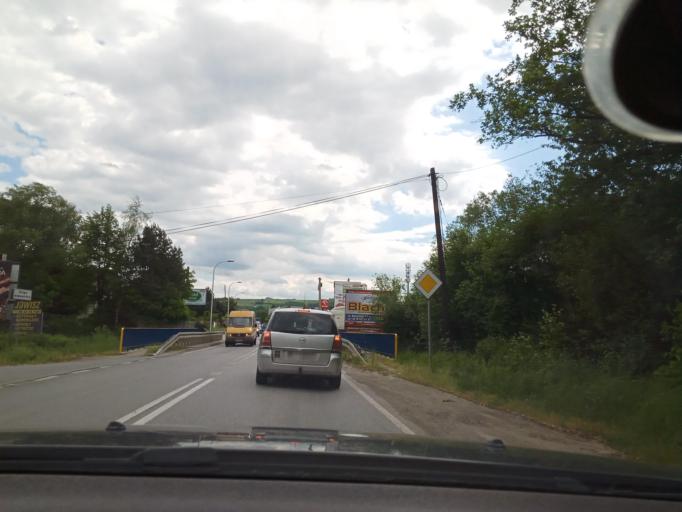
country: PL
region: Lesser Poland Voivodeship
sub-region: Powiat limanowski
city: Limanowa
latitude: 49.7317
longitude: 20.3991
